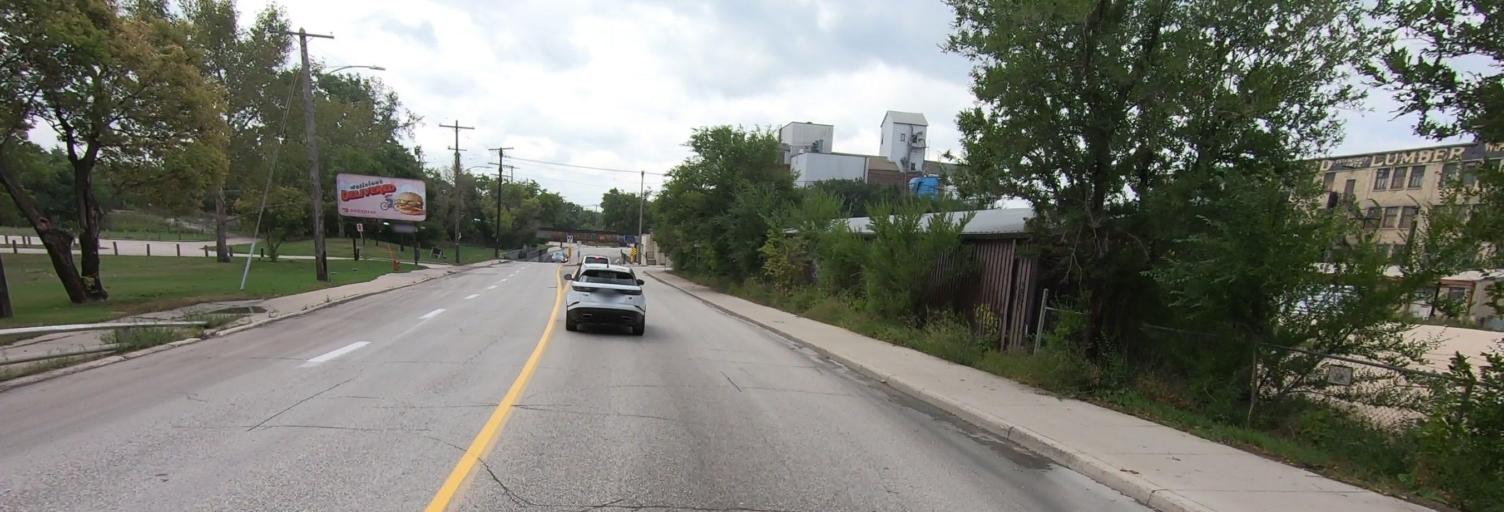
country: CA
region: Manitoba
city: Winnipeg
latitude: 49.9045
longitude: -97.1145
